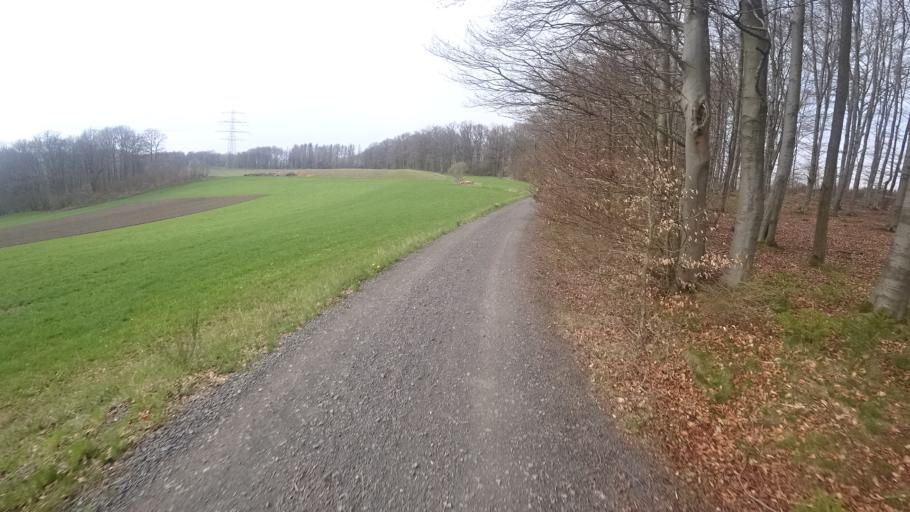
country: DE
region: Rheinland-Pfalz
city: Scheuerfeld
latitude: 50.7763
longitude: 7.8411
